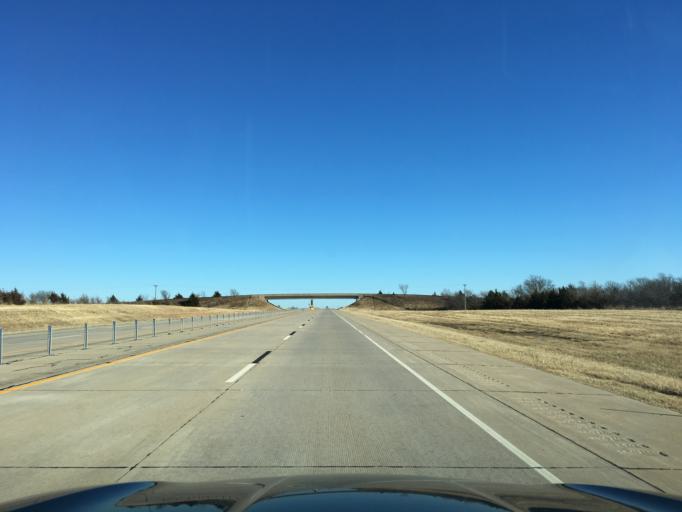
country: US
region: Oklahoma
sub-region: Payne County
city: Yale
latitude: 36.2250
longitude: -96.6633
